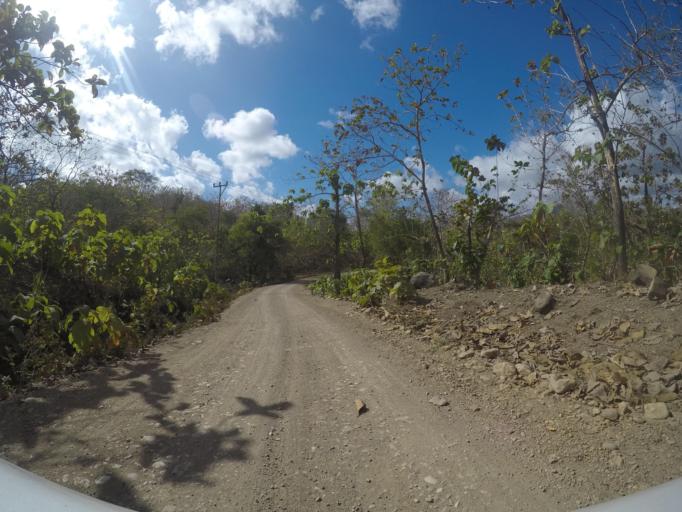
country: TL
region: Lautem
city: Lospalos
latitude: -8.5267
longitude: 126.8411
